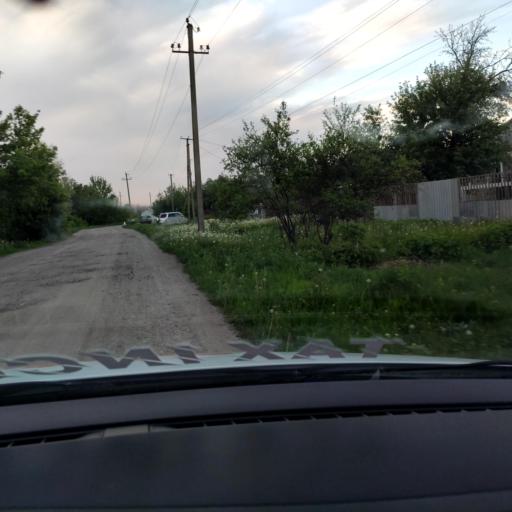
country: RU
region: Voronezj
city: Kolodeznyy
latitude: 51.4367
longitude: 39.2319
